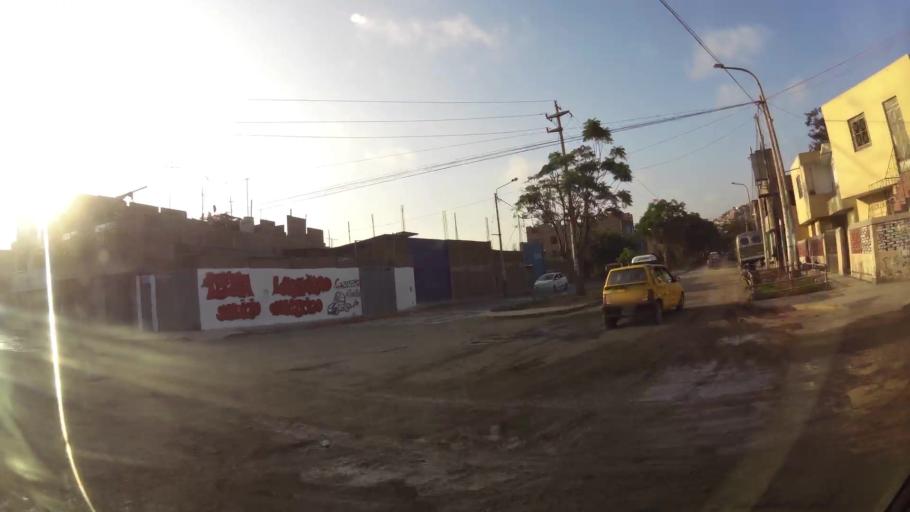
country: PE
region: La Libertad
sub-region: Provincia de Trujillo
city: El Porvenir
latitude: -8.0935
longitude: -78.9961
